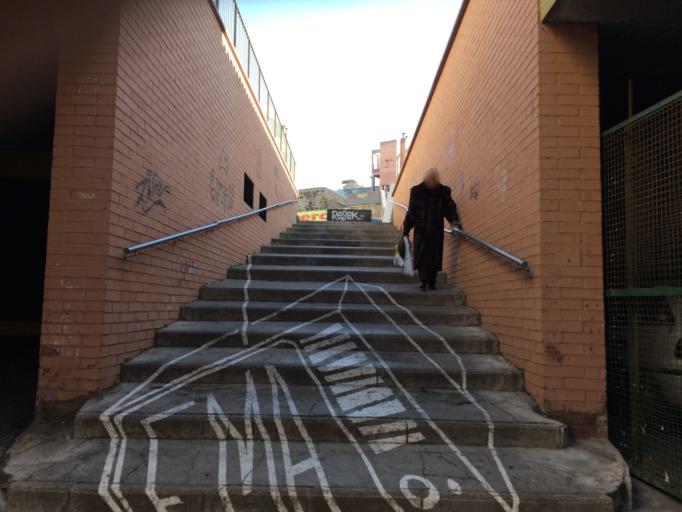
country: ES
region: Catalonia
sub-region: Provincia de Barcelona
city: Manresa
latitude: 41.7248
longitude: 1.8251
